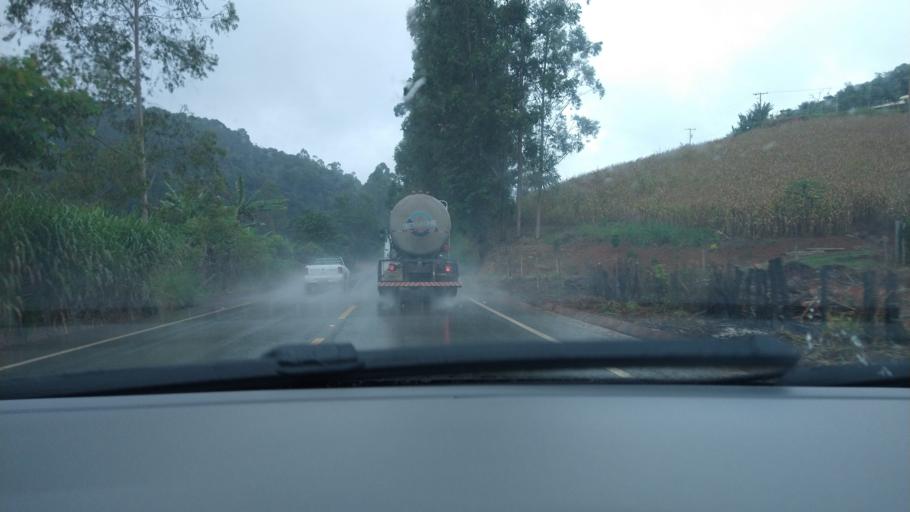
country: BR
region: Minas Gerais
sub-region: Vicosa
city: Vicosa
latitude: -20.5893
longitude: -42.8806
